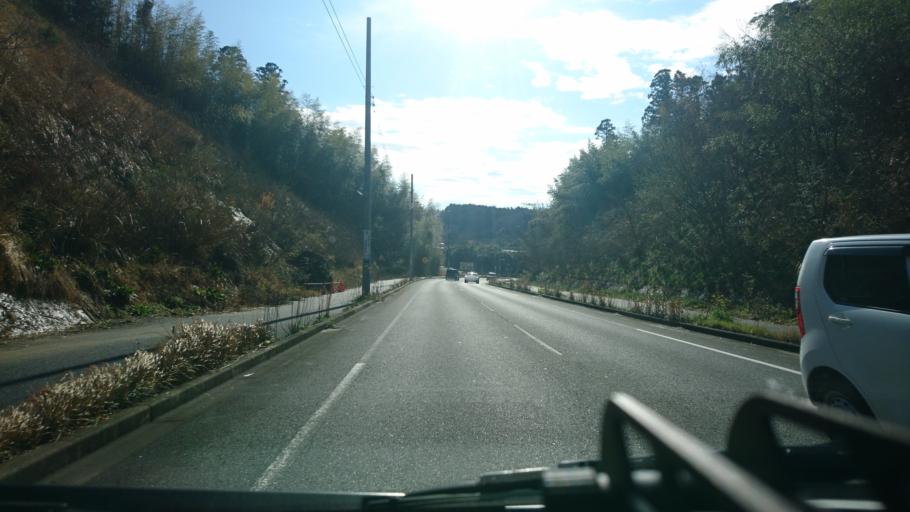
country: JP
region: Chiba
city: Kisarazu
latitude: 35.3541
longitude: 139.9402
